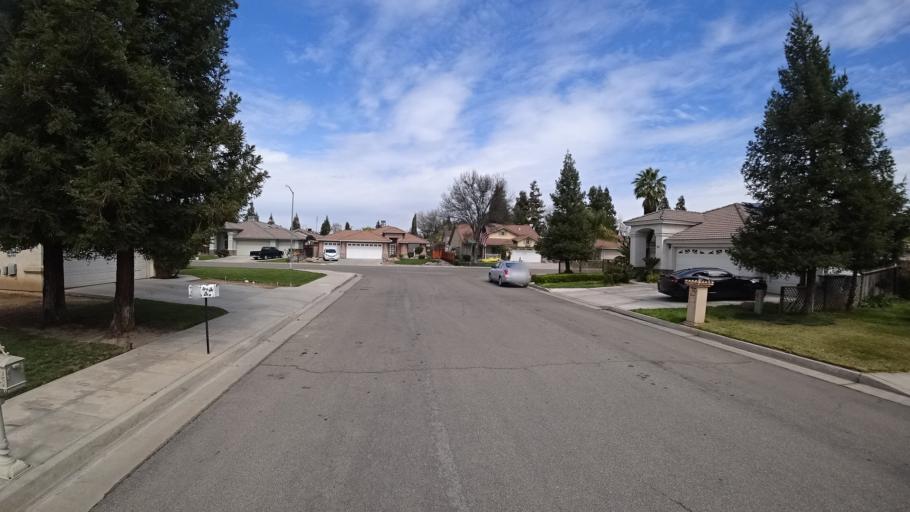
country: US
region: California
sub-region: Fresno County
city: Biola
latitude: 36.8414
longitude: -119.8914
